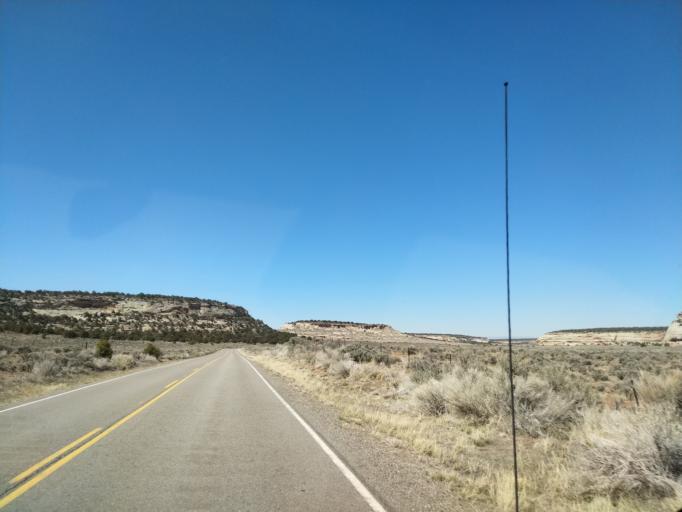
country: US
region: Colorado
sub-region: Mesa County
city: Fruita
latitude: 38.9832
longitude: -108.8021
